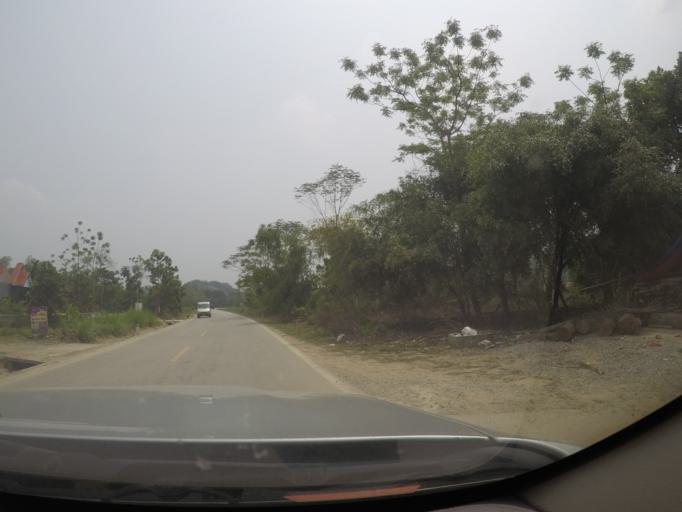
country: VN
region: Thanh Hoa
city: Thi Tran Yen Cat
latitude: 19.7408
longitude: 105.4245
